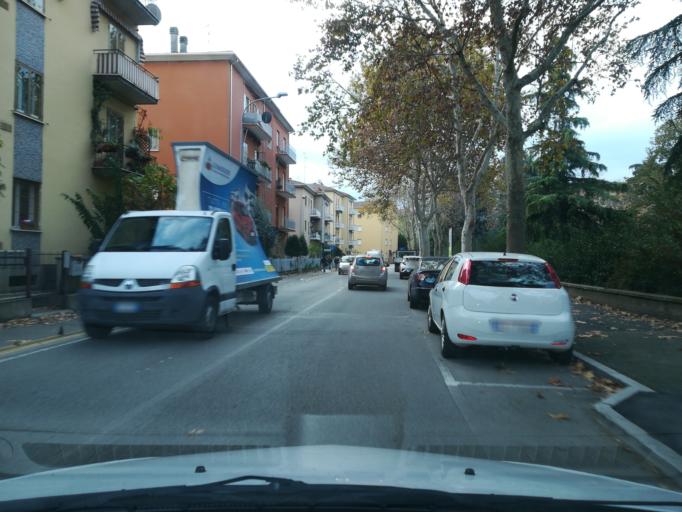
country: IT
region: Emilia-Romagna
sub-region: Provincia di Bologna
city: Imola
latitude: 44.3488
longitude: 11.7187
